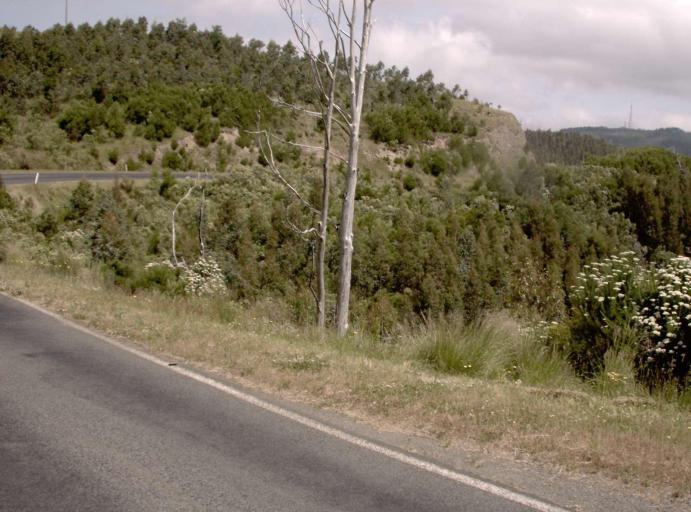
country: AU
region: Victoria
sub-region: Latrobe
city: Traralgon
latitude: -38.3645
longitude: 146.5653
